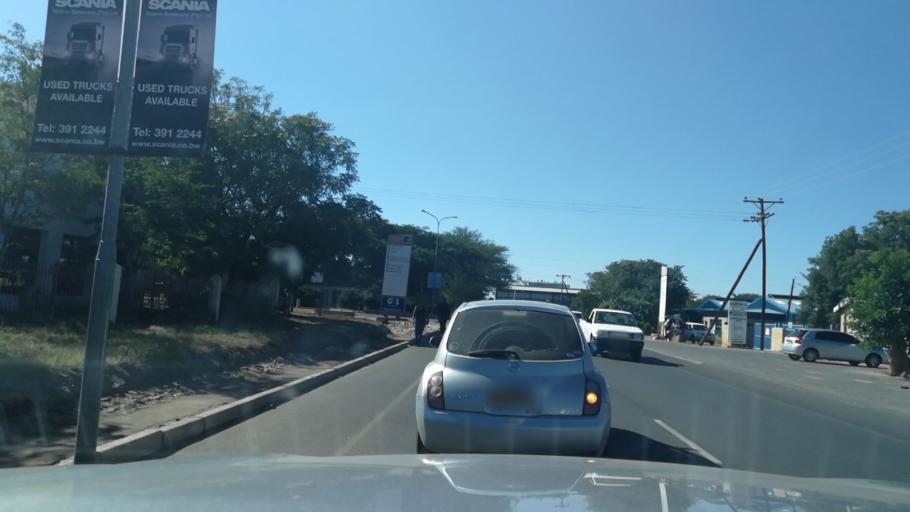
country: BW
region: South East
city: Gaborone
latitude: -24.6918
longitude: 25.8858
